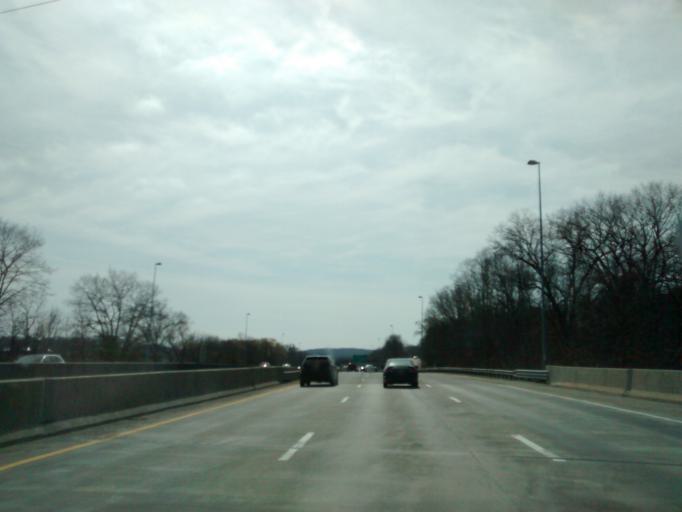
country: US
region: Massachusetts
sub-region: Worcester County
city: Auburn
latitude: 42.2099
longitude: -71.8376
